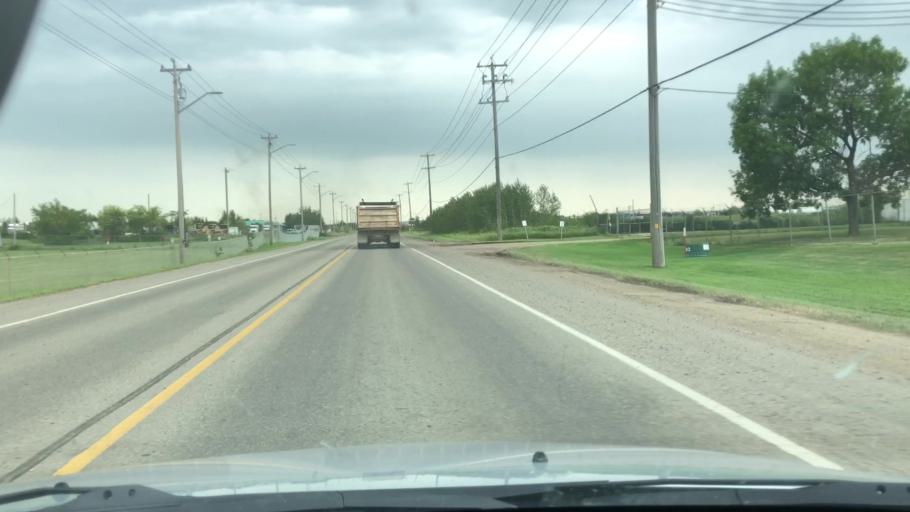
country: CA
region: Alberta
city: Sherwood Park
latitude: 53.5254
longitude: -113.3939
